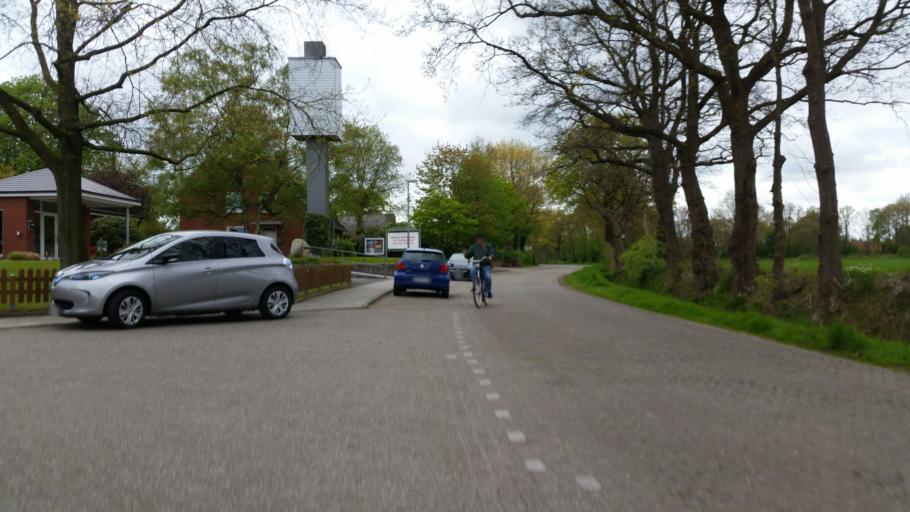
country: DE
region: Lower Saxony
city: Aurich
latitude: 53.4783
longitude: 7.4437
